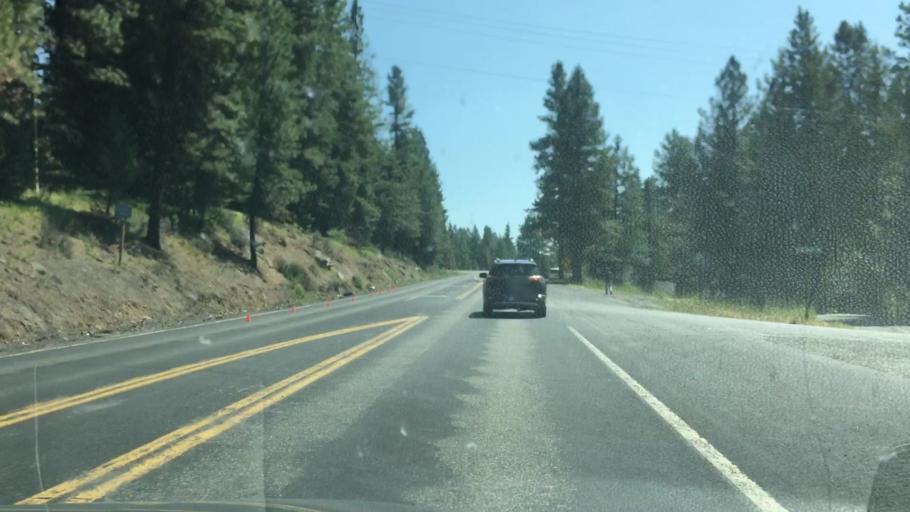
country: US
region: Idaho
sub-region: Valley County
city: McCall
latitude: 44.9342
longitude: -116.1653
